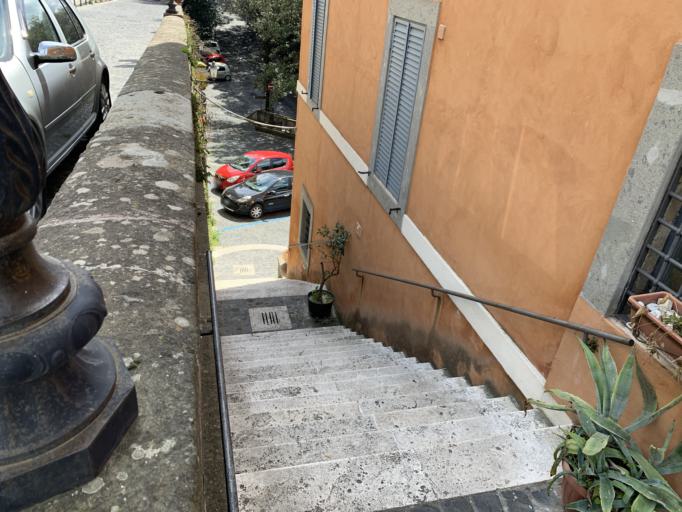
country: IT
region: Latium
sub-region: Citta metropolitana di Roma Capitale
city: Castel Gandolfo
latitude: 41.7445
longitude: 12.6513
